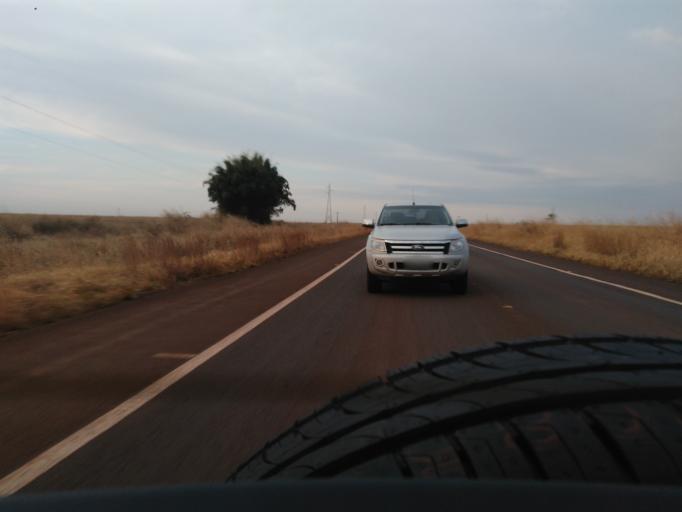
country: BR
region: Mato Grosso do Sul
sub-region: Dourados
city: Dourados
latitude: -22.2900
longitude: -55.0291
